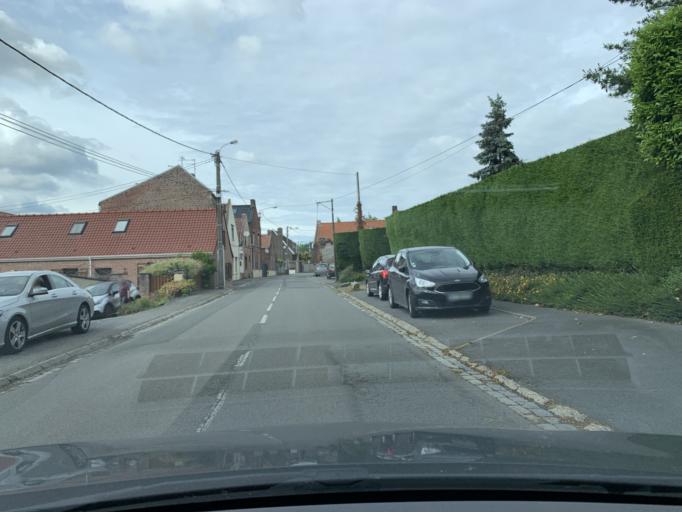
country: FR
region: Nord-Pas-de-Calais
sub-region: Departement du Nord
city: Lewarde
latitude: 50.3387
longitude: 3.1627
